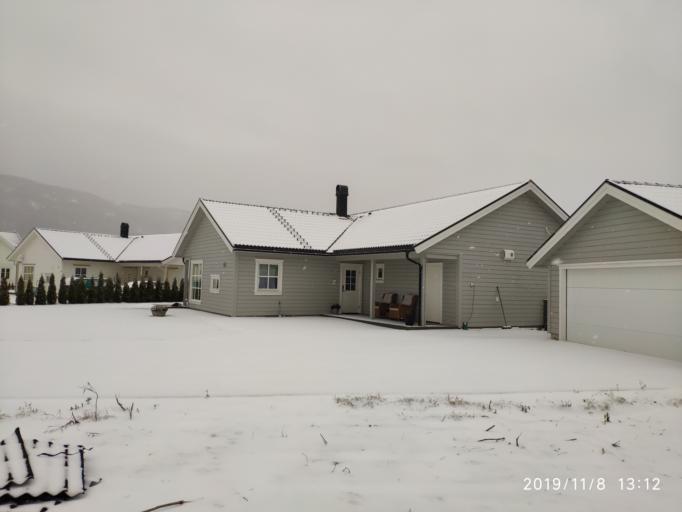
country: NO
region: Buskerud
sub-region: Kongsberg
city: Kongsberg
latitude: 59.5539
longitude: 9.8058
